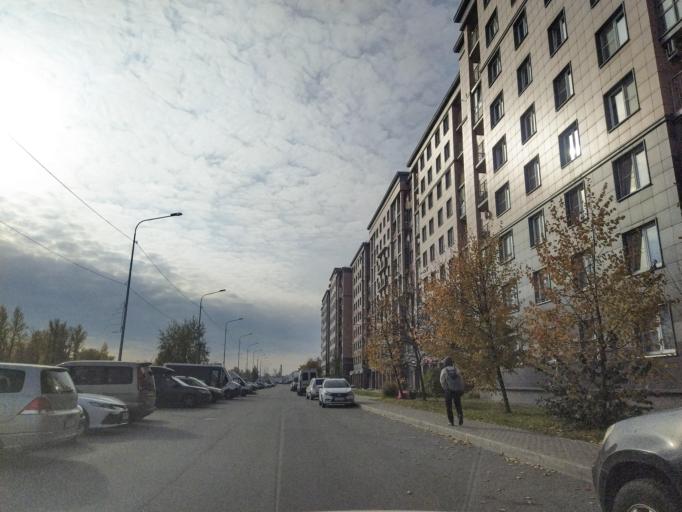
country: RU
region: St.-Petersburg
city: Tyarlevo
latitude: 59.7379
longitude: 30.4752
